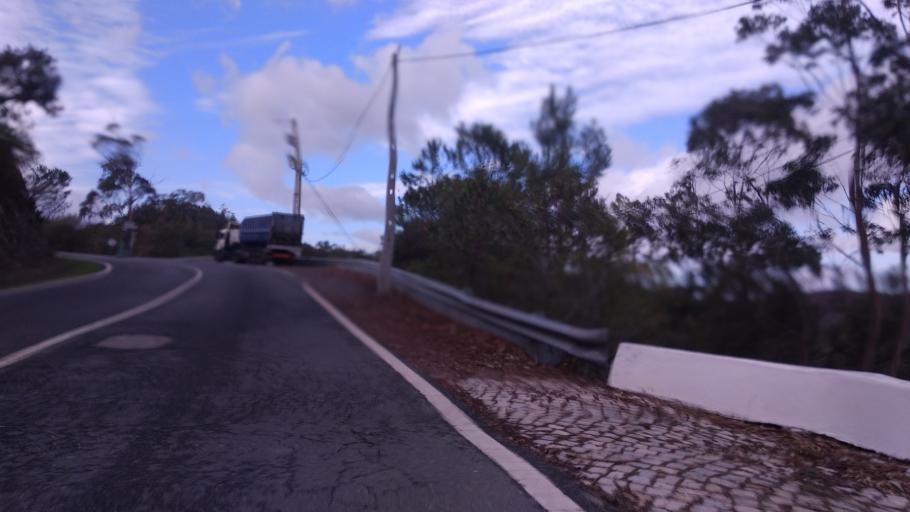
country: PT
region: Faro
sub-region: Sao Bras de Alportel
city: Sao Bras de Alportel
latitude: 37.1800
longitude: -7.9109
